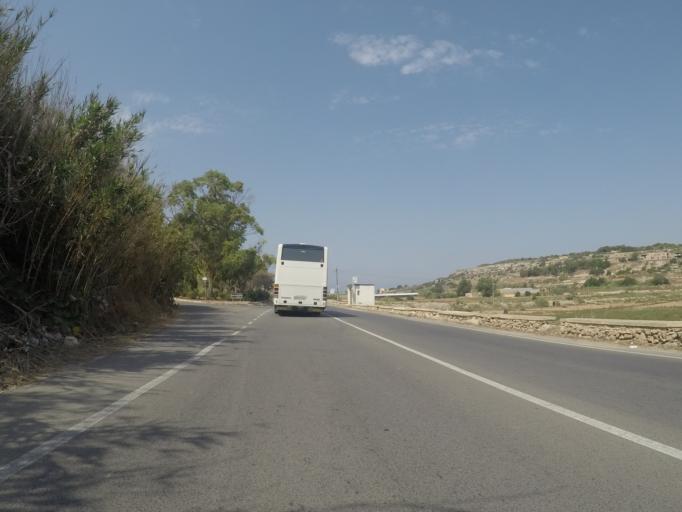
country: MT
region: Il-Mellieha
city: Mellieha
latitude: 35.9411
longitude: 14.3768
